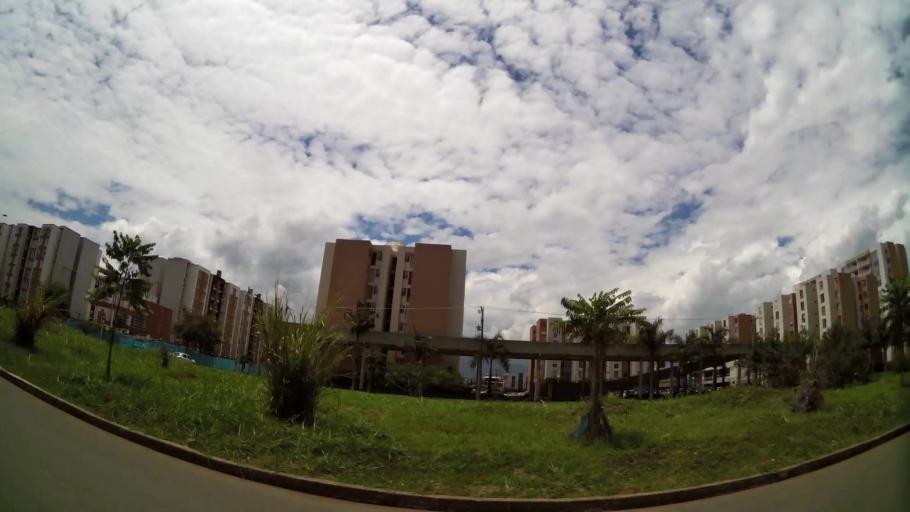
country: CO
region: Valle del Cauca
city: Cali
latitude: 3.3711
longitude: -76.5163
